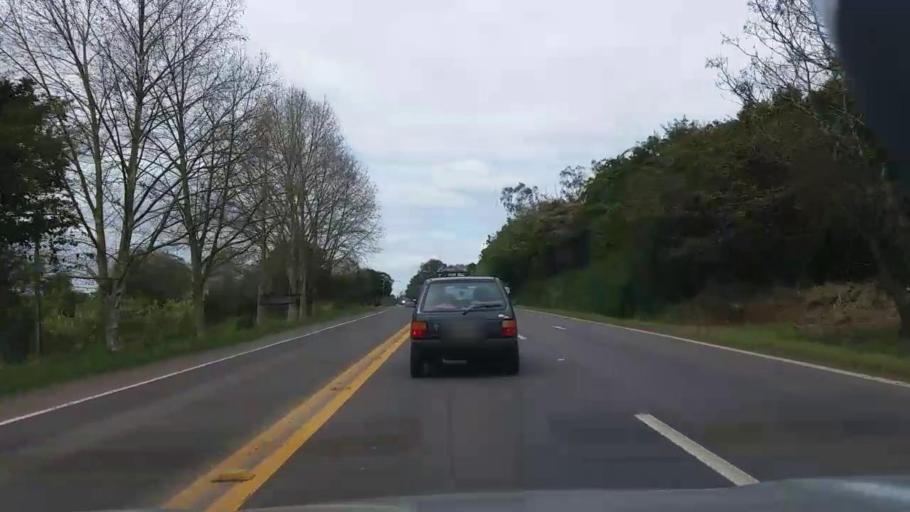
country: BR
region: Rio Grande do Sul
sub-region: Lajeado
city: Lajeado
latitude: -29.4305
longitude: -52.0142
